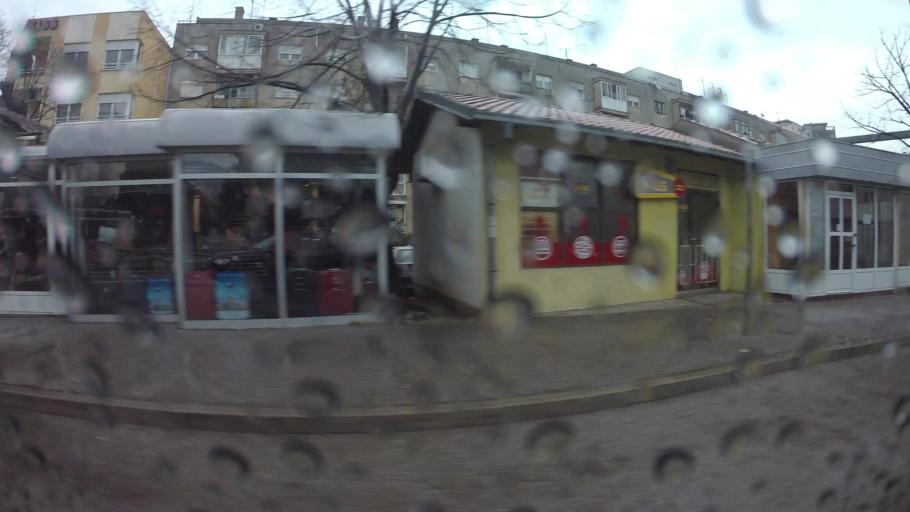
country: BA
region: Federation of Bosnia and Herzegovina
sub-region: Hercegovacko-Bosanski Kanton
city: Mostar
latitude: 43.3491
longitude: 17.7990
